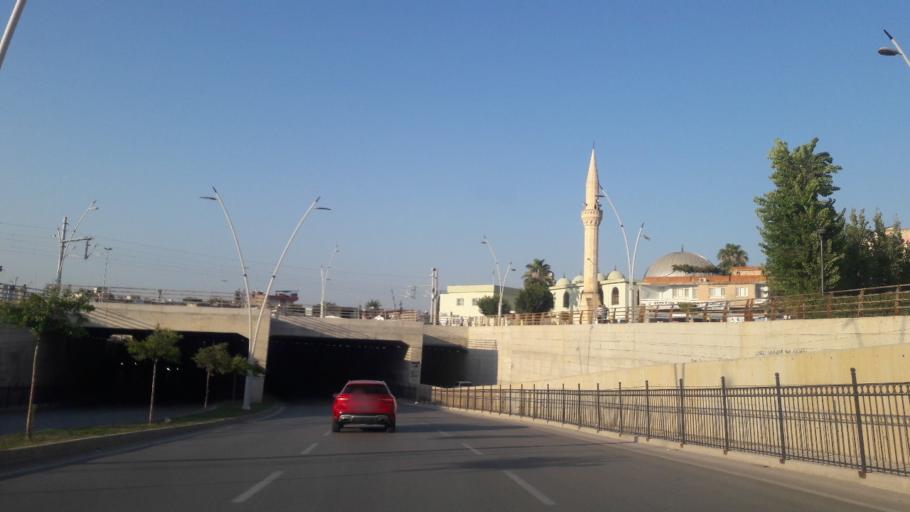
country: TR
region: Adana
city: Seyhan
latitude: 36.9962
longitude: 35.3012
